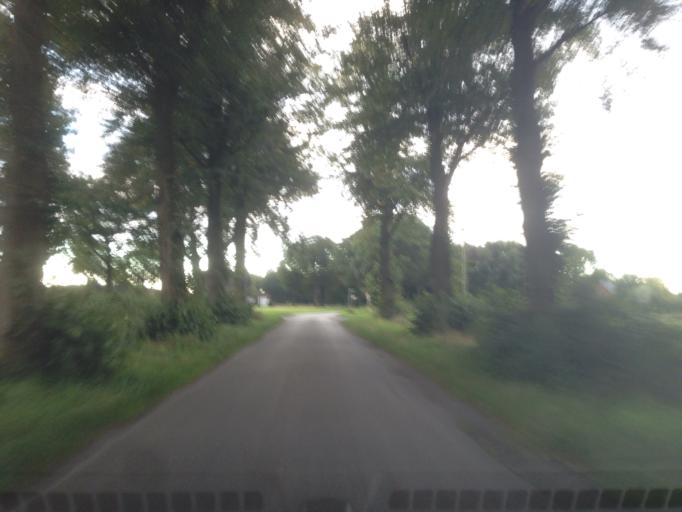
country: DE
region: North Rhine-Westphalia
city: Olfen
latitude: 51.7519
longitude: 7.3904
